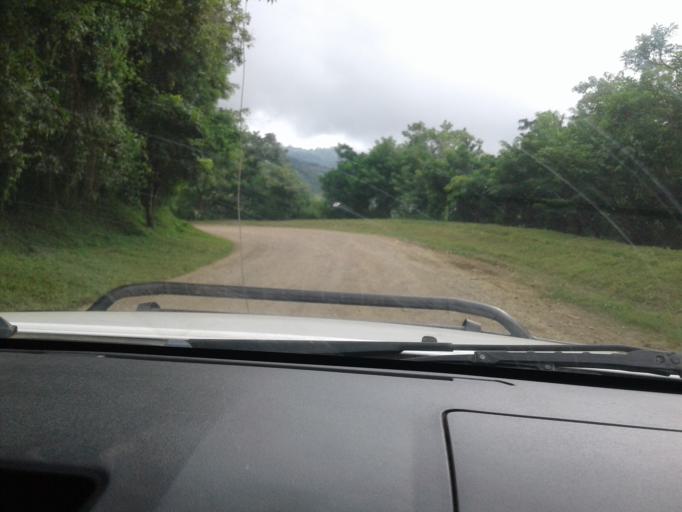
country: NI
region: Matagalpa
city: San Ramon
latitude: 12.9054
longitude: -85.8000
